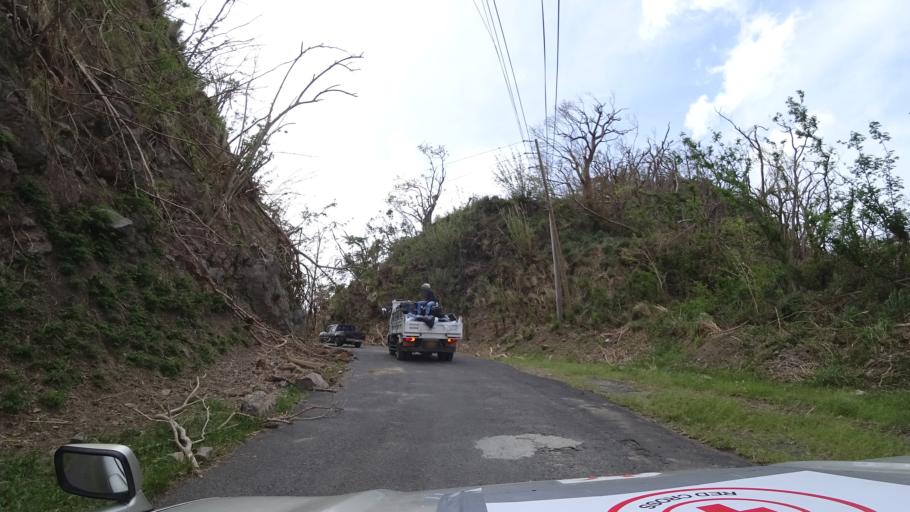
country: DM
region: Saint Mark
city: Soufriere
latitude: 15.2392
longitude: -61.3656
